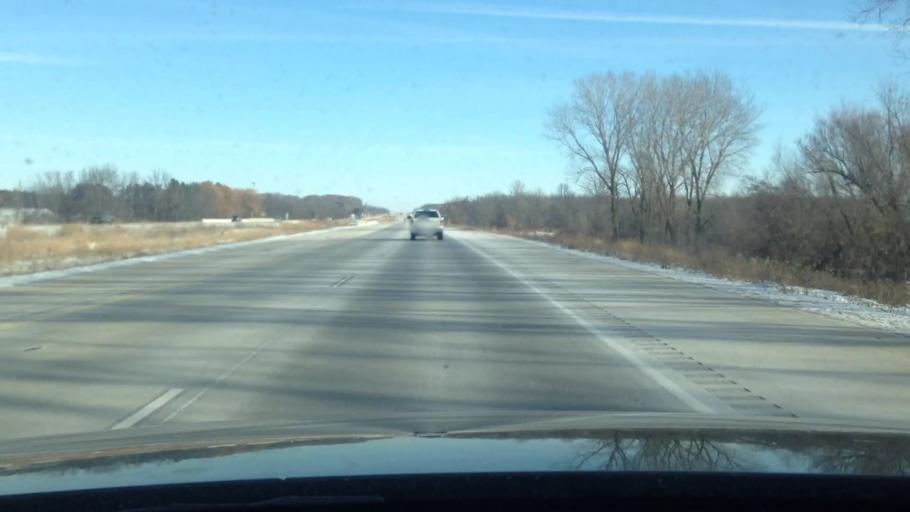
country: US
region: Wisconsin
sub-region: Waukesha County
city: Mukwonago
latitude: 42.8659
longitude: -88.2984
